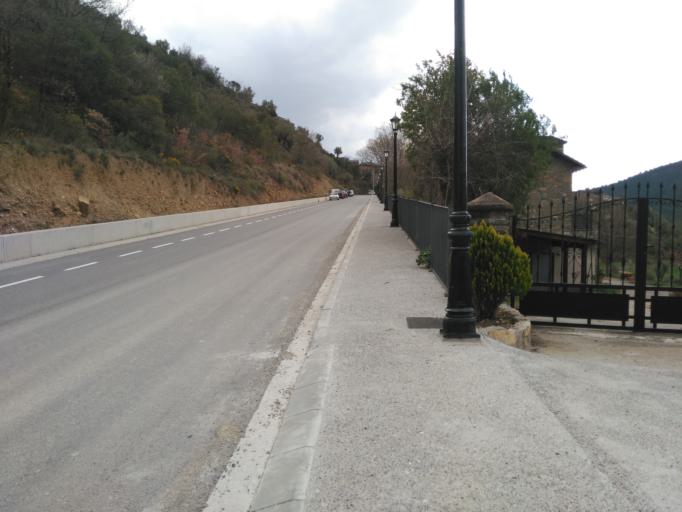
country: ES
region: Aragon
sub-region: Provincia de Huesca
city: Boltana
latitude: 42.4491
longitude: 0.0660
